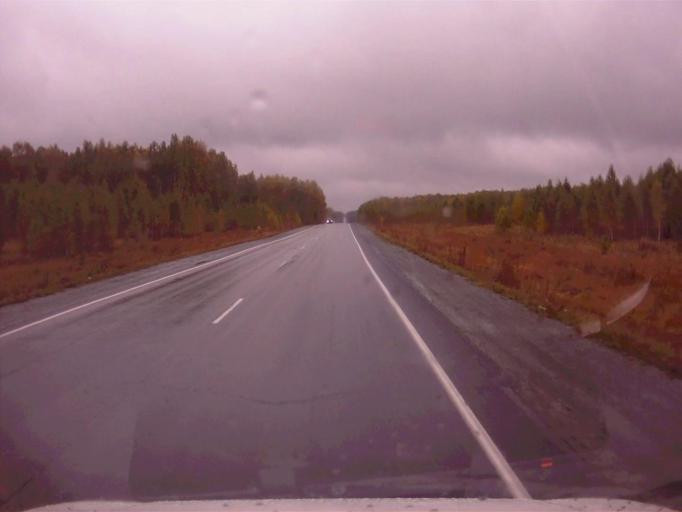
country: RU
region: Chelyabinsk
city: Tayginka
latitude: 55.5076
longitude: 60.6372
